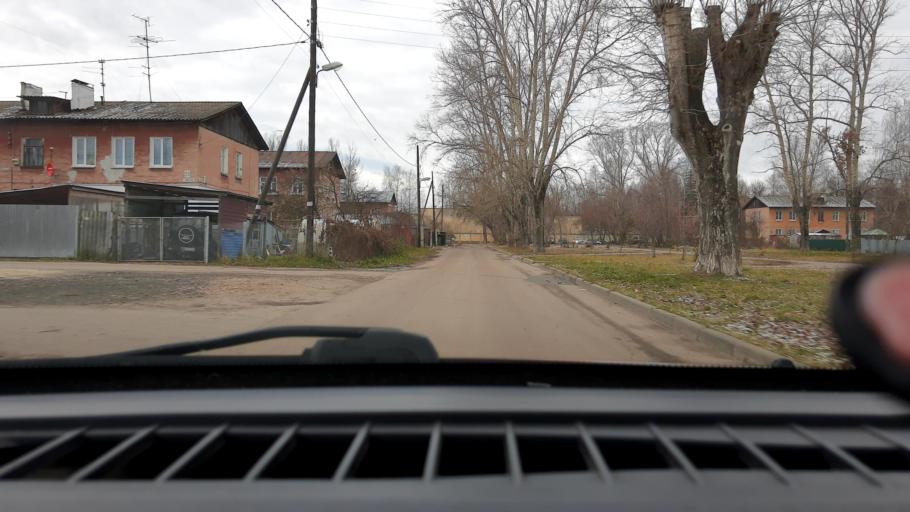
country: RU
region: Nizjnij Novgorod
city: Gorbatovka
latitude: 56.3811
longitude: 43.7856
